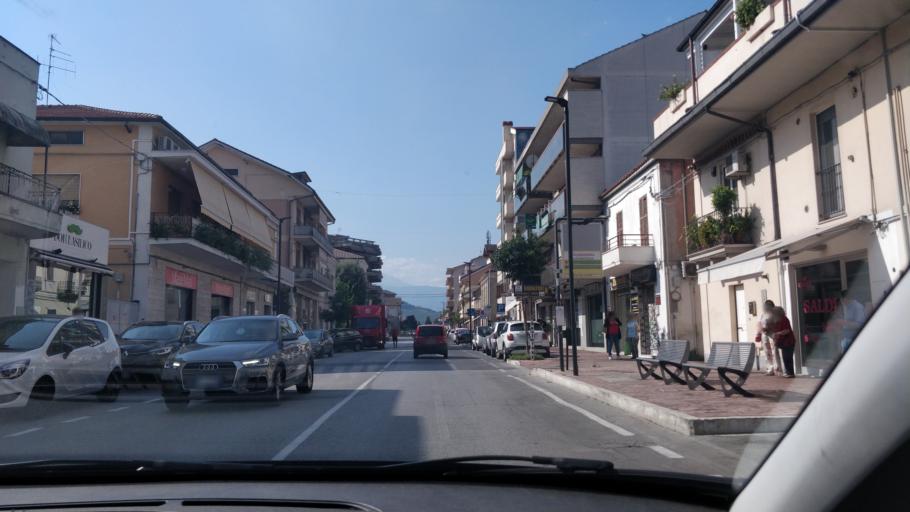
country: IT
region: Abruzzo
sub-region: Provincia di Chieti
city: Chieti
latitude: 42.3562
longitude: 14.1386
